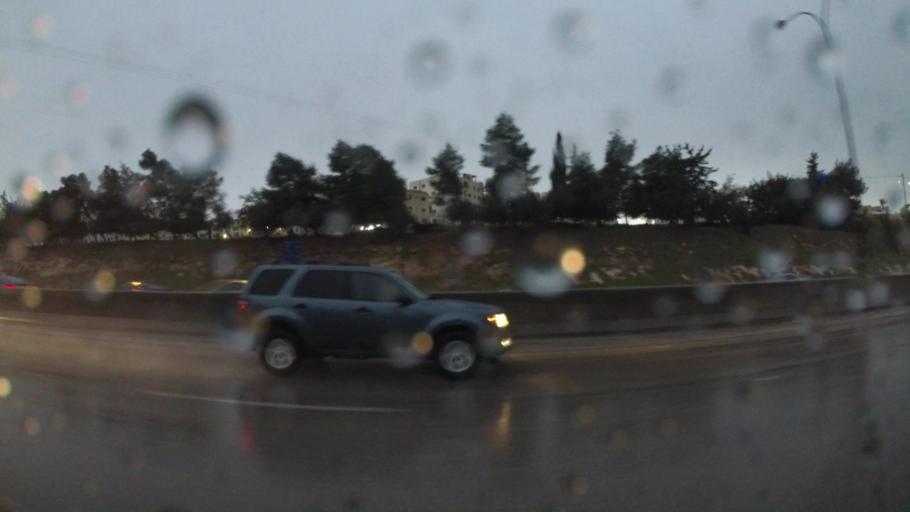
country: JO
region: Amman
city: Umm as Summaq
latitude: 31.9048
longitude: 35.8691
